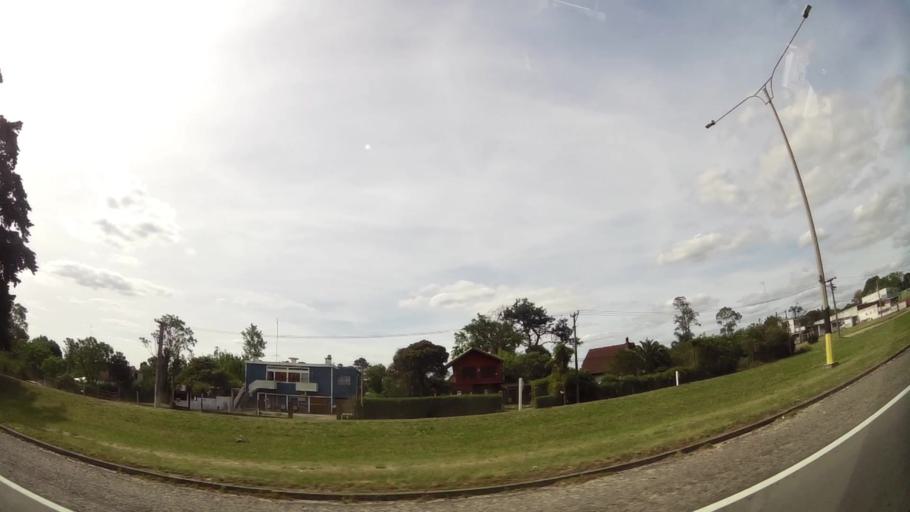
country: UY
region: Canelones
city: Empalme Olmos
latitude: -34.7788
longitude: -55.8653
